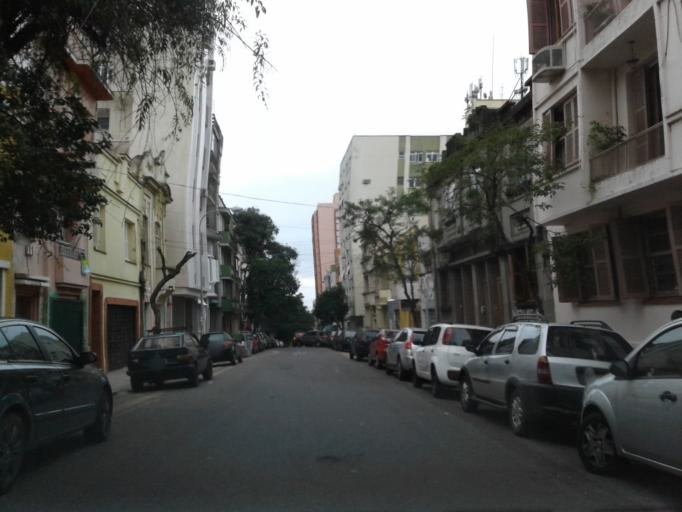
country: BR
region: Rio Grande do Sul
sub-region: Porto Alegre
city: Porto Alegre
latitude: -30.0335
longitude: -51.2369
